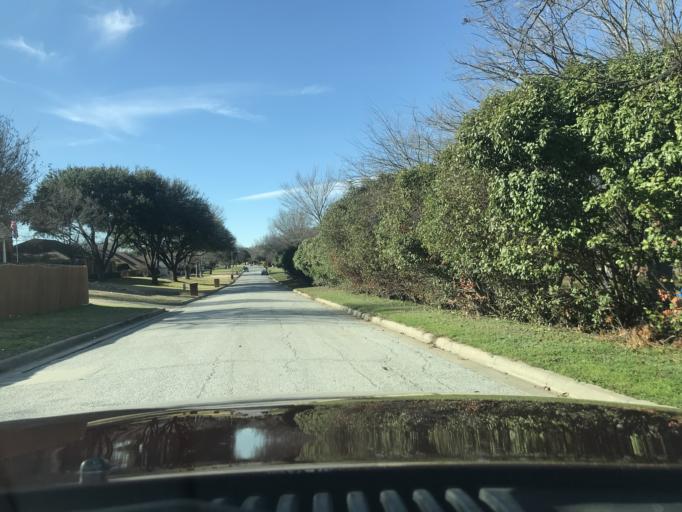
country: US
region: Texas
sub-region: Tarrant County
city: Edgecliff Village
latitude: 32.6557
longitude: -97.3436
